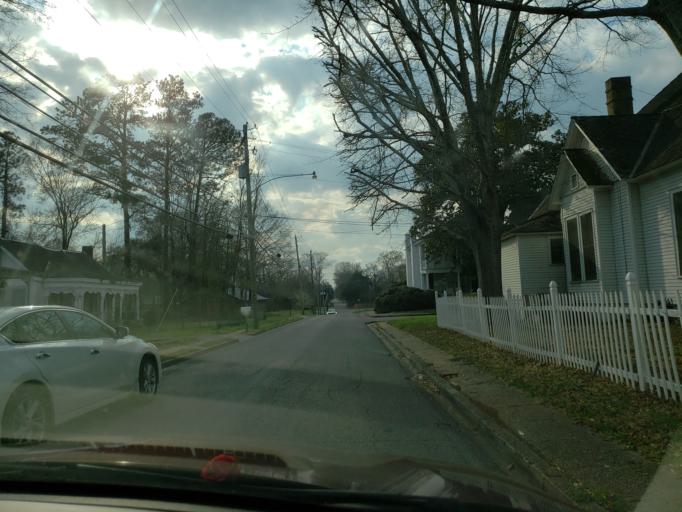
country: US
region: Alabama
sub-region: Hale County
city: Greensboro
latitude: 32.7030
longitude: -87.5932
